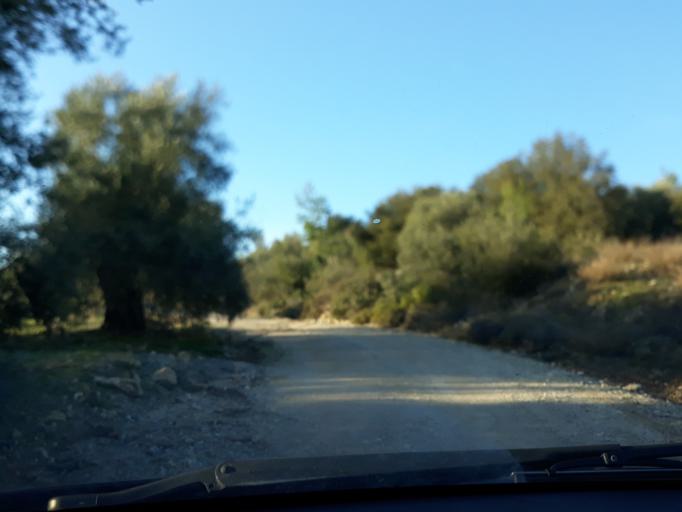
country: GR
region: Central Greece
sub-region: Nomos Voiotias
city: Asopia
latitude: 38.2649
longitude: 23.5337
